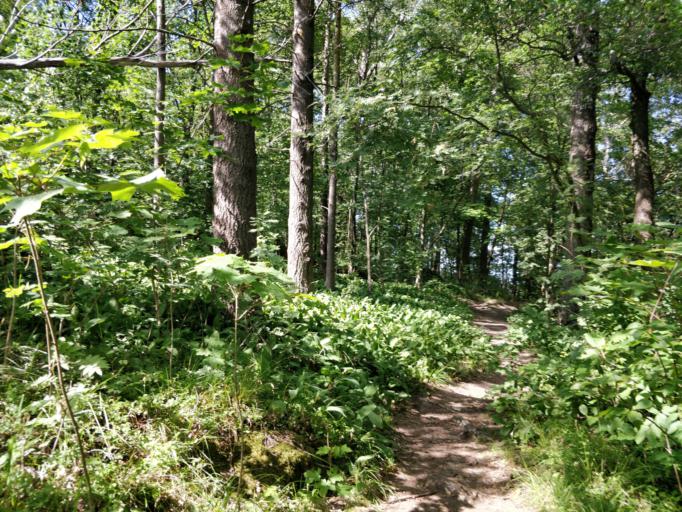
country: FI
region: Uusimaa
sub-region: Helsinki
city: Helsinki
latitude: 60.2041
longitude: 24.9954
